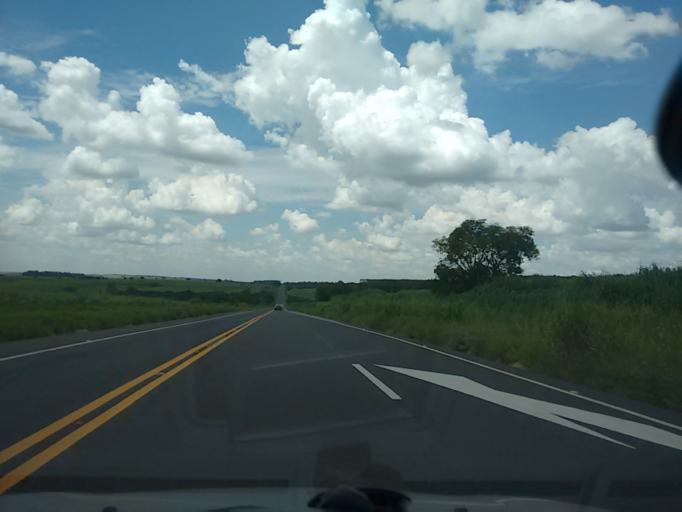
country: BR
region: Sao Paulo
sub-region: Osvaldo Cruz
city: Osvaldo Cruz
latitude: -21.8641
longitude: -50.8491
